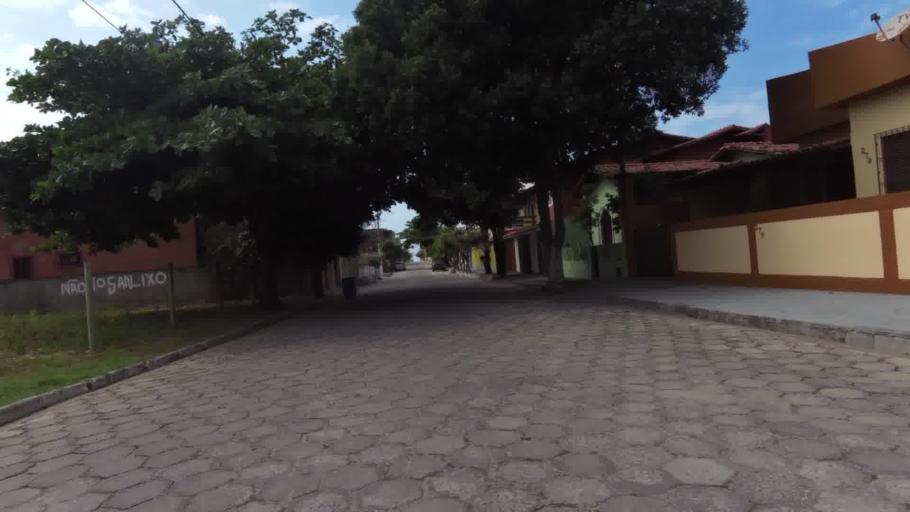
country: BR
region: Espirito Santo
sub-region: Marataizes
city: Marataizes
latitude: -21.0333
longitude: -40.8165
